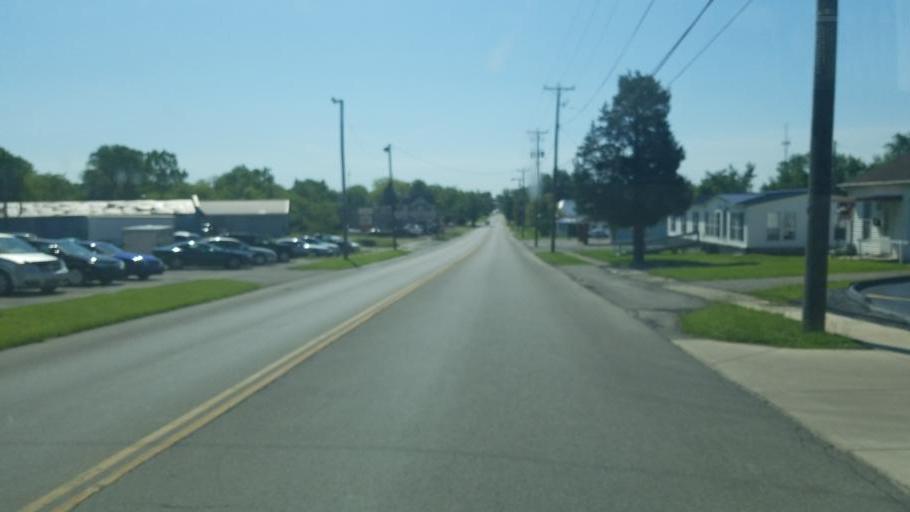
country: US
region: Ohio
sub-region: Hardin County
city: Kenton
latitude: 40.6497
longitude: -83.6198
